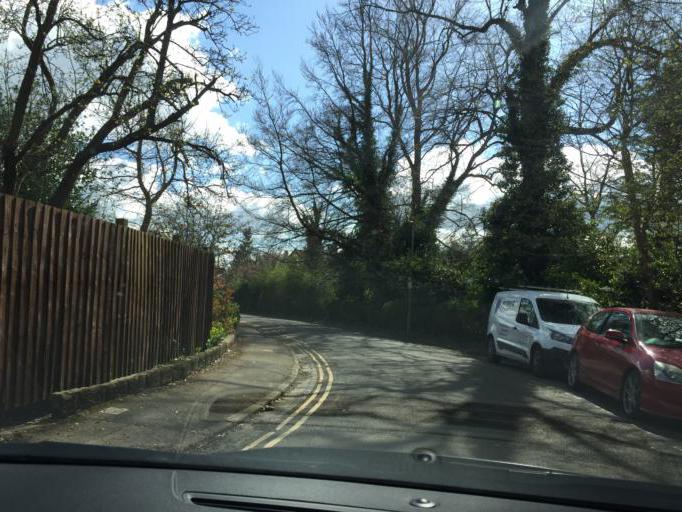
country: GB
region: England
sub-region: Oxfordshire
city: Cowley
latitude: 51.7570
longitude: -1.2186
